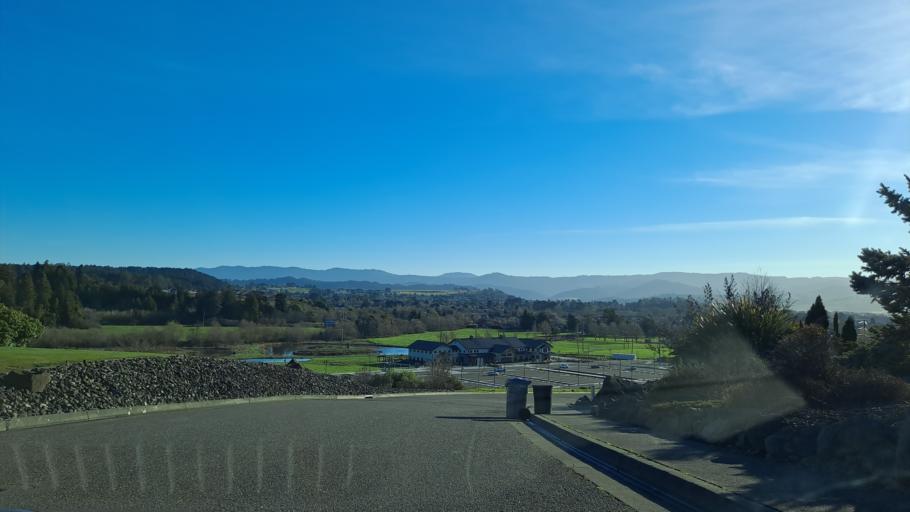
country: US
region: California
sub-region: Humboldt County
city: Fortuna
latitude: 40.5965
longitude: -124.1334
